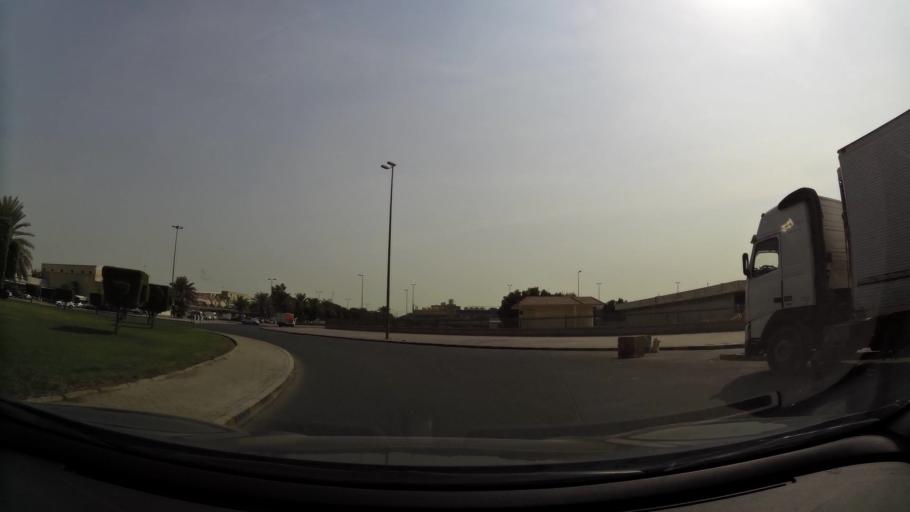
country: KW
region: Al Asimah
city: Ar Rabiyah
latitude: 29.3260
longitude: 47.9272
